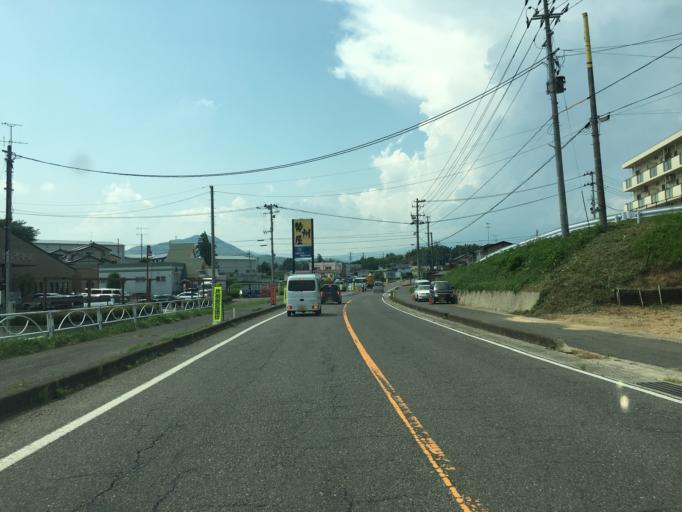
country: JP
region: Fukushima
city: Motomiya
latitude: 37.5028
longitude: 140.3977
